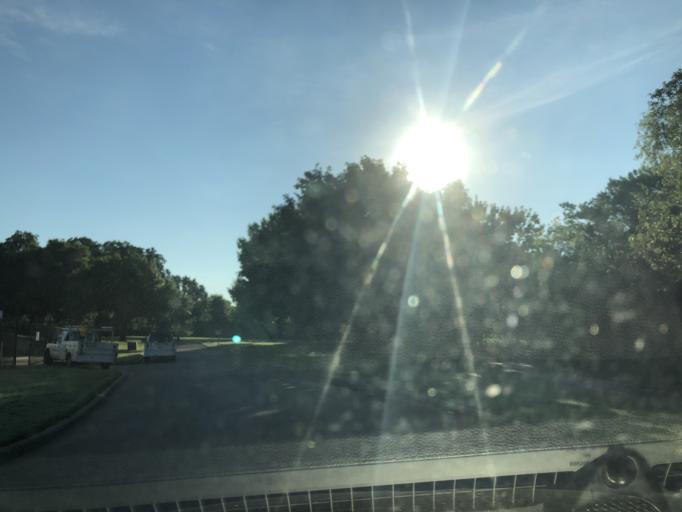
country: US
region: Texas
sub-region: Dallas County
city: Garland
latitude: 32.8463
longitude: -96.6148
